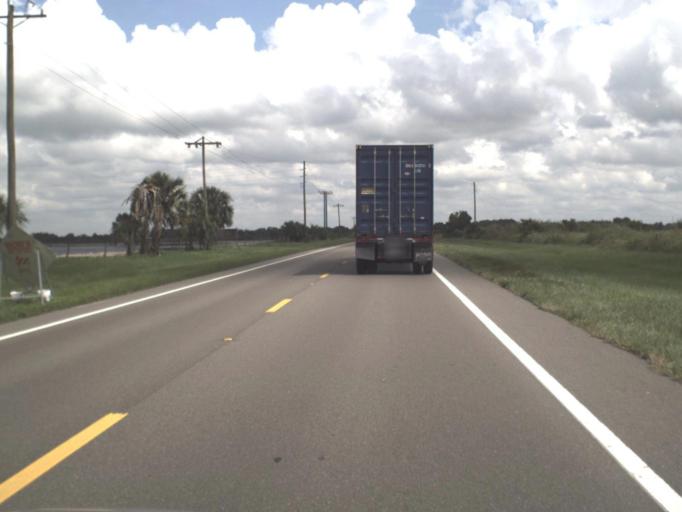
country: US
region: Florida
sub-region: Sarasota County
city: The Meadows
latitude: 27.4755
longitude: -82.3701
